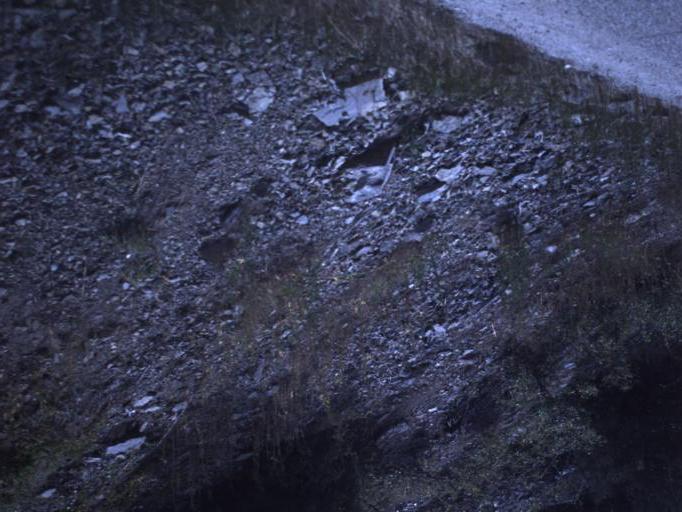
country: US
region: Utah
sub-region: Cache County
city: North Logan
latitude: 41.8218
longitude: -111.6130
